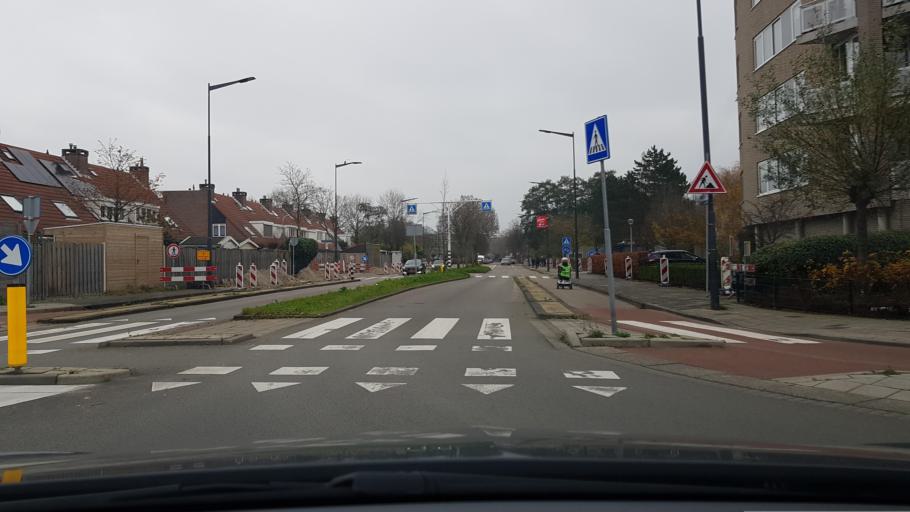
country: NL
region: North Holland
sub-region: Gemeente Heemstede
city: Heemstede
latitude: 52.3542
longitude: 4.6547
